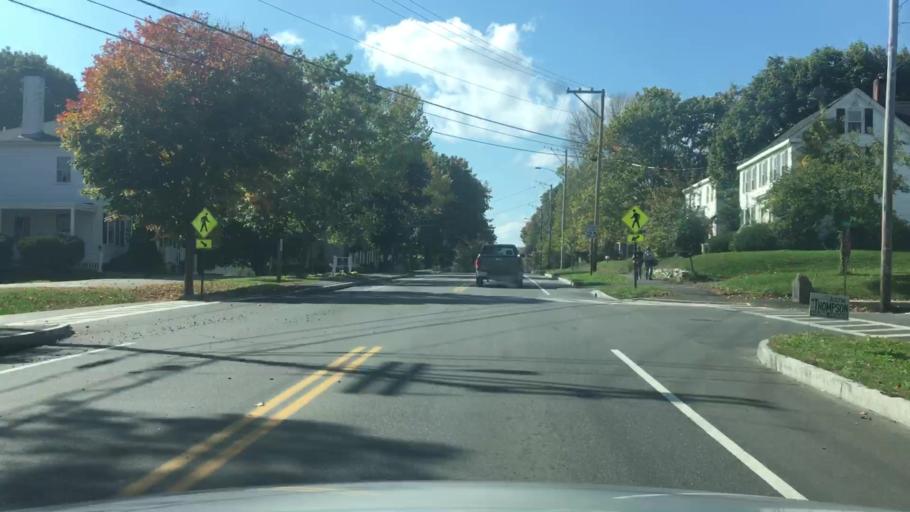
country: US
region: Maine
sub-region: Knox County
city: Thomaston
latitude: 44.0800
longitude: -69.1770
